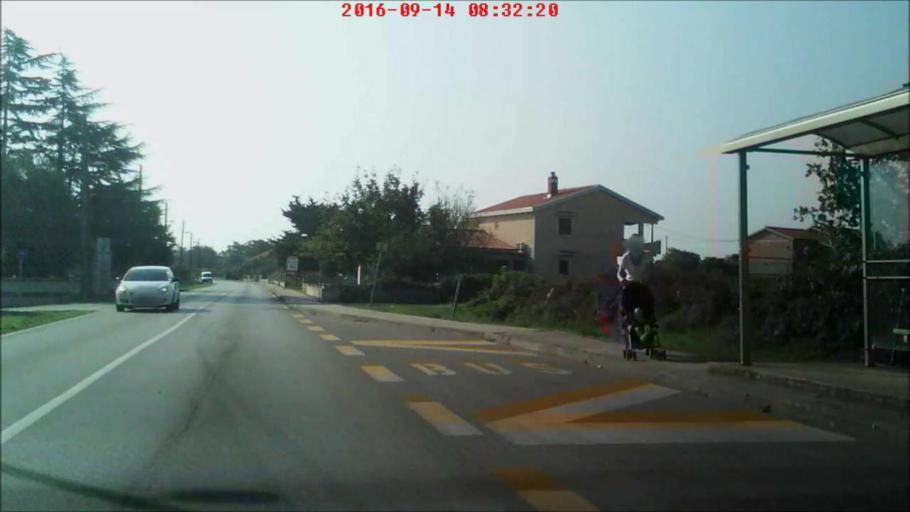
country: HR
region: Zadarska
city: Policnik
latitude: 44.1639
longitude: 15.3056
